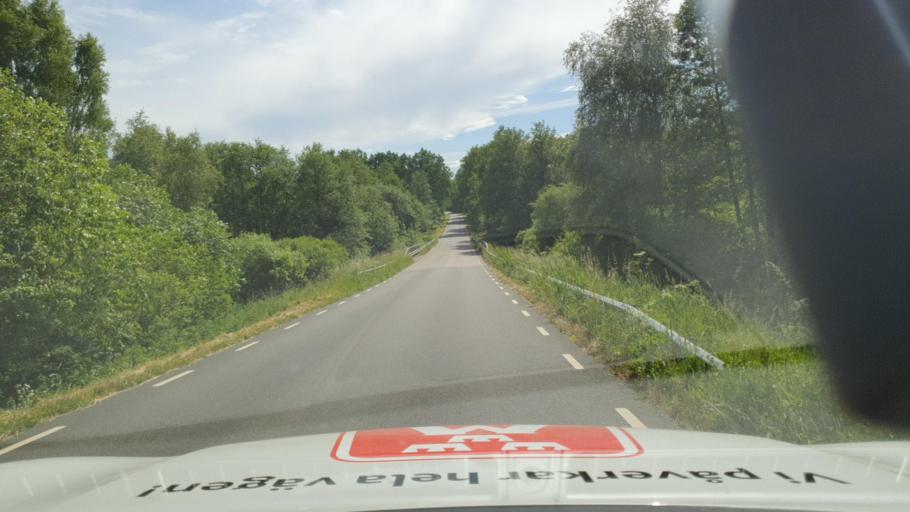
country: SE
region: Skane
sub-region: Tomelilla Kommun
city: Tomelilla
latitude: 55.6922
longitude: 13.9502
